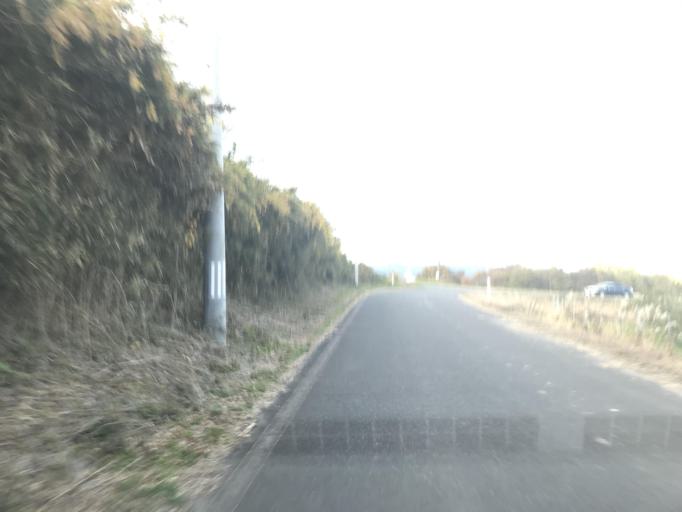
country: JP
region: Iwate
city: Ichinoseki
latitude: 38.8824
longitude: 141.1622
